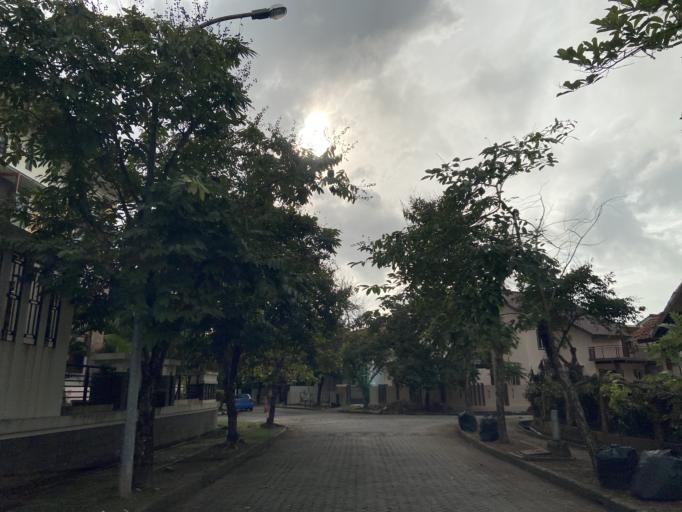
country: SG
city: Singapore
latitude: 1.1104
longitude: 104.0245
